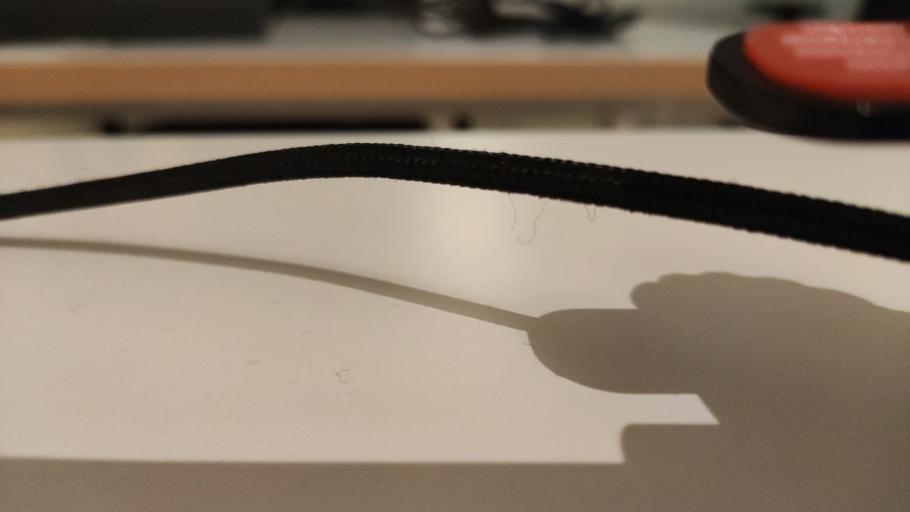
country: RU
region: Moskovskaya
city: Skoropuskovskiy
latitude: 56.3771
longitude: 38.0933
